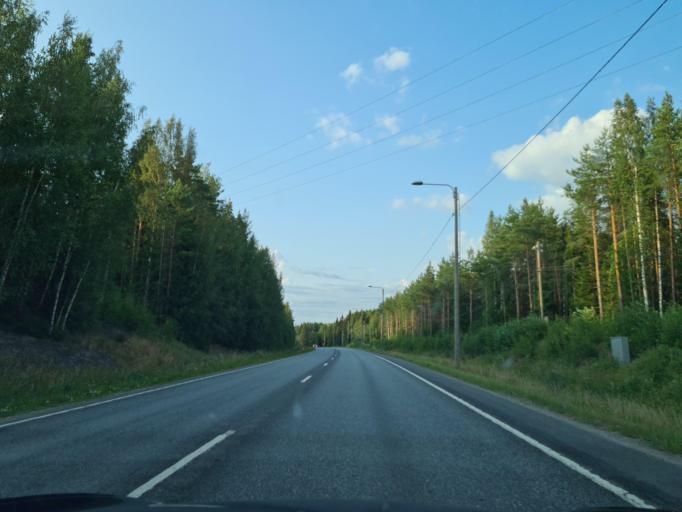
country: FI
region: Southern Ostrobothnia
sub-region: Seinaejoki
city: Kauhava
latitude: 63.0739
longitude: 23.0547
